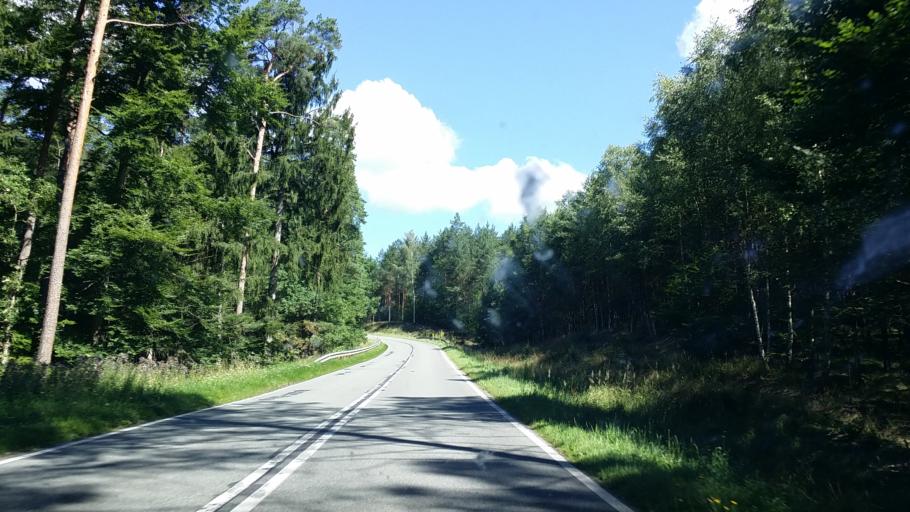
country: PL
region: West Pomeranian Voivodeship
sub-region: Powiat drawski
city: Kalisz Pomorski
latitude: 53.3915
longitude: 15.8501
